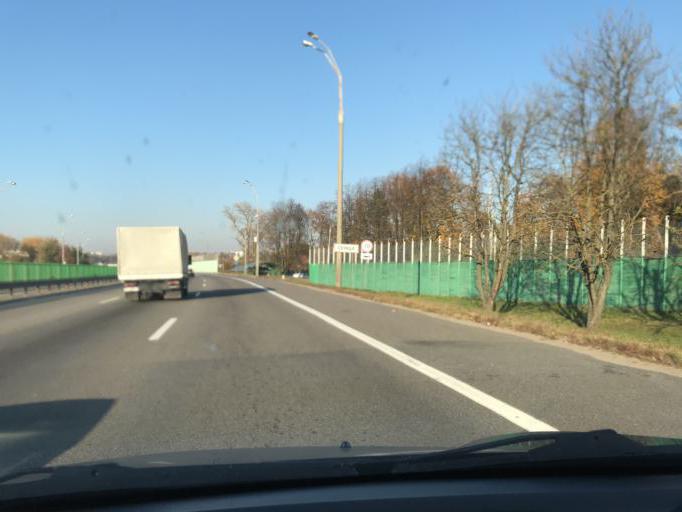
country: BY
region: Minsk
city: Syenitsa
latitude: 53.8240
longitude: 27.5337
